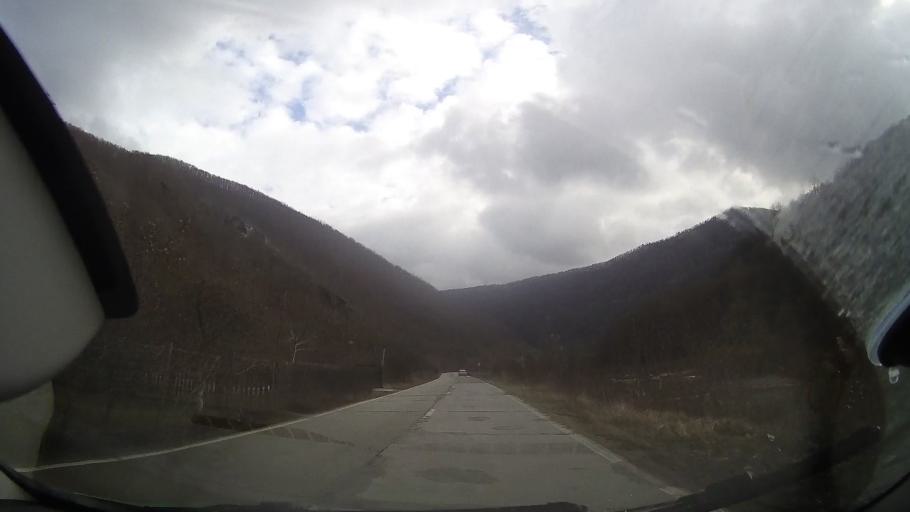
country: RO
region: Alba
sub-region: Comuna Rimetea
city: Rimetea
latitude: 46.5095
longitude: 23.5675
